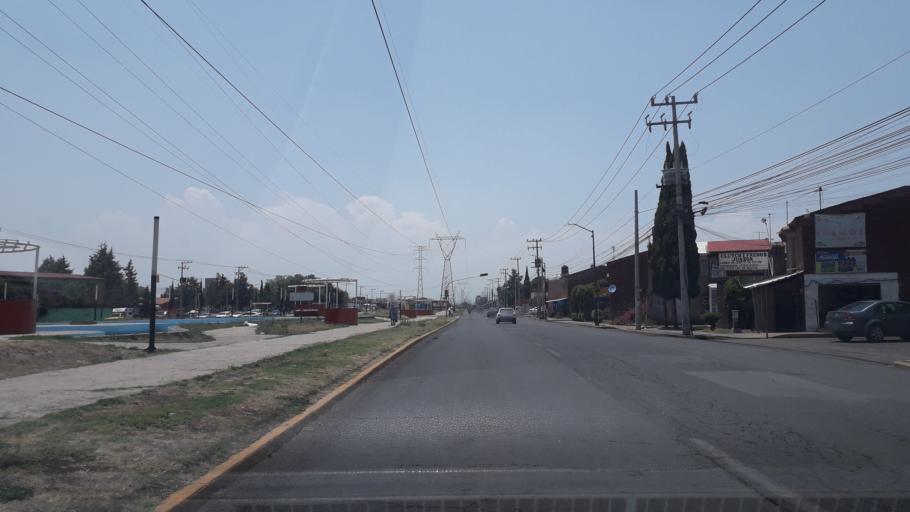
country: MX
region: Mexico
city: Santiago Teyahualco
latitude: 19.6417
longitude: -99.1214
